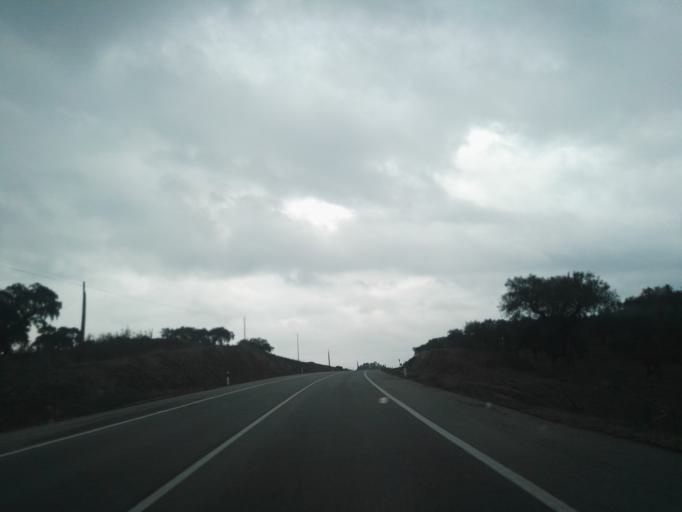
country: PT
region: Portalegre
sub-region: Portalegre
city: Alegrete
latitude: 39.1741
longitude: -7.3365
